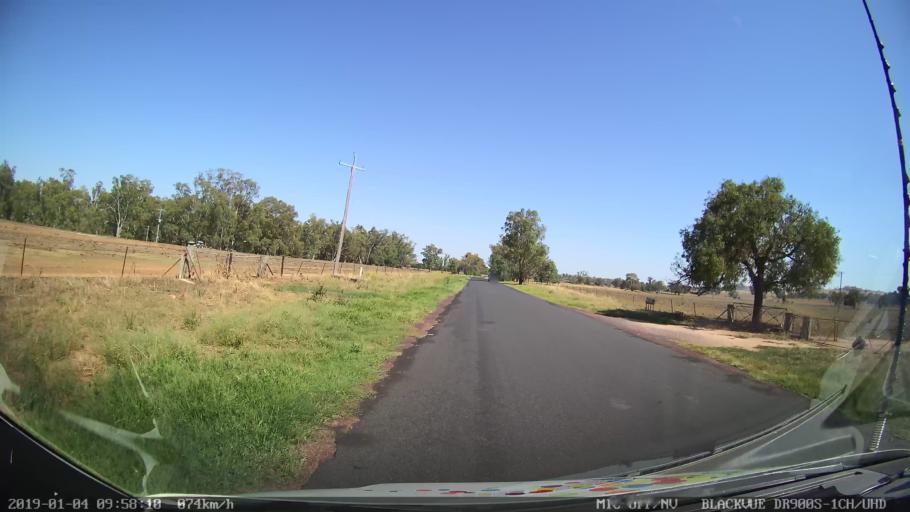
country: AU
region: New South Wales
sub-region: Cabonne
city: Canowindra
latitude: -33.5210
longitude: 148.3964
